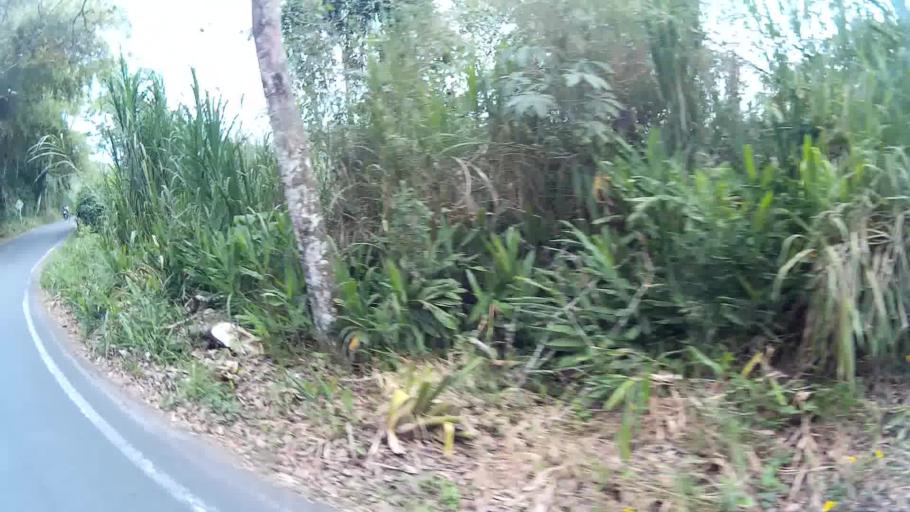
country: CO
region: Risaralda
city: Marsella
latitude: 4.9148
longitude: -75.7378
